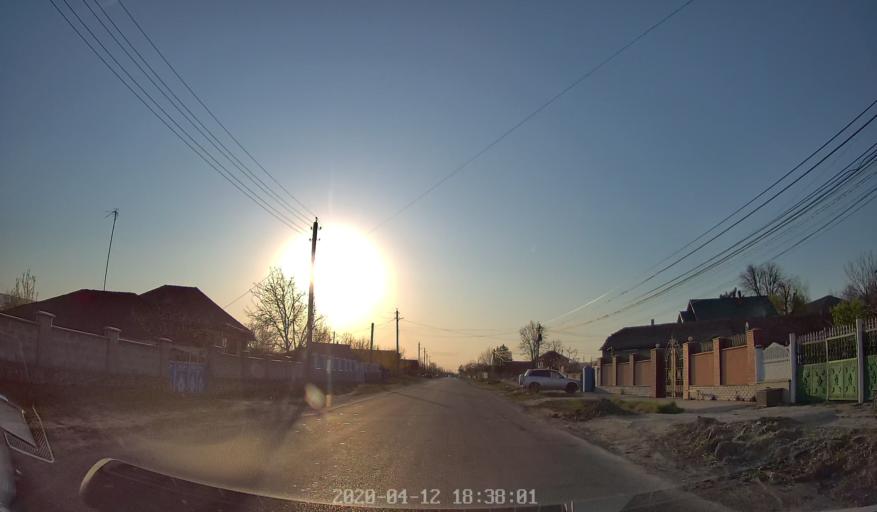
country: MD
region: Chisinau
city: Vadul lui Voda
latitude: 47.1231
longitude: 29.0064
